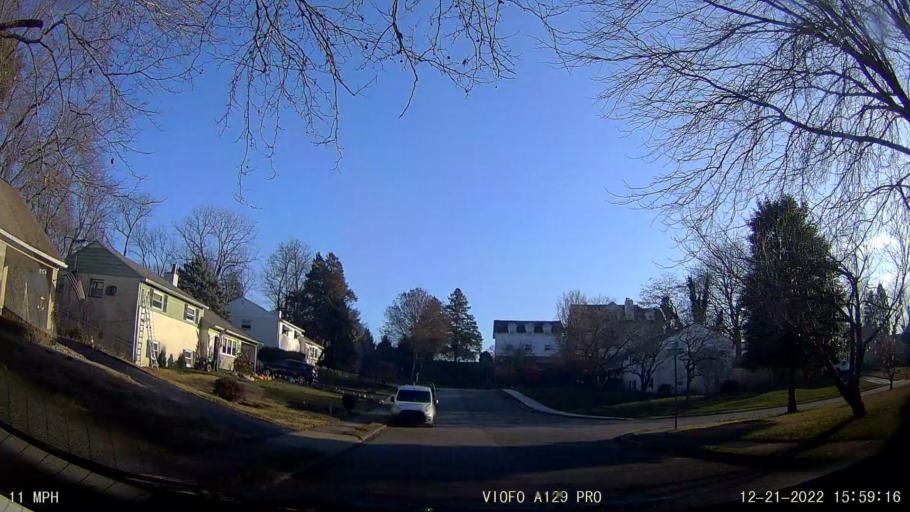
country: US
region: Pennsylvania
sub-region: Montgomery County
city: King of Prussia
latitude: 40.1045
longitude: -75.3774
